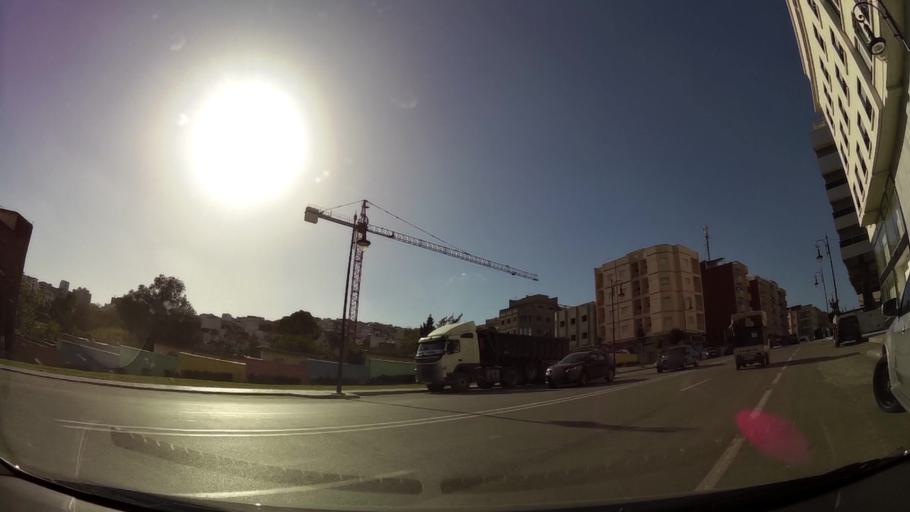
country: MA
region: Tanger-Tetouan
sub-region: Tanger-Assilah
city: Tangier
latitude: 35.7432
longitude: -5.8066
